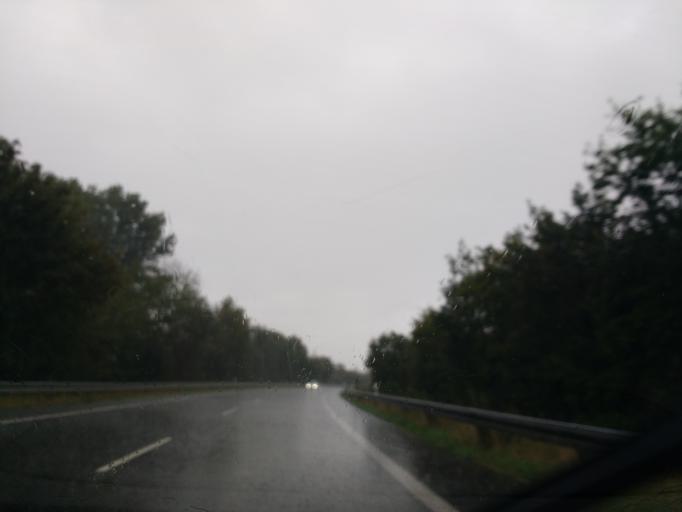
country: DE
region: North Rhine-Westphalia
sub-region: Regierungsbezirk Munster
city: Ostbevern
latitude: 52.1168
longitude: 7.8595
